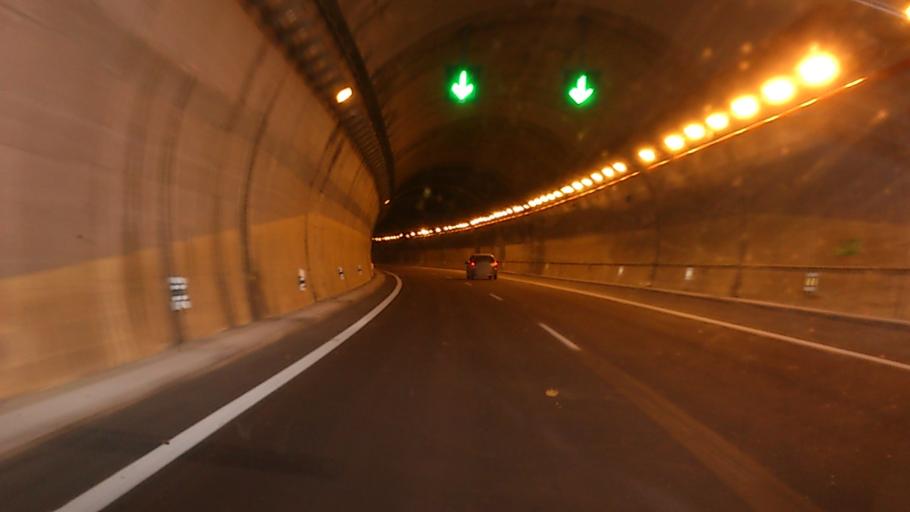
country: ES
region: Valencia
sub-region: Provincia de Valencia
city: L'Olleria
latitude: 38.9270
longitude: -0.5756
